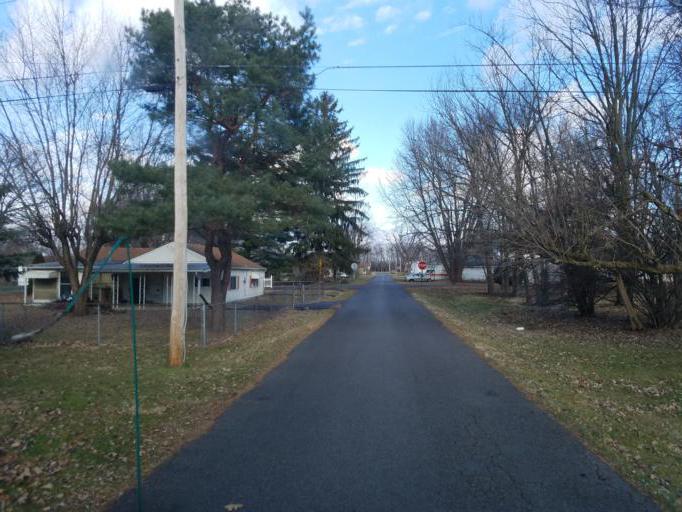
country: US
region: Ohio
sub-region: Marion County
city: Marion
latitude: 40.5716
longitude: -83.1574
